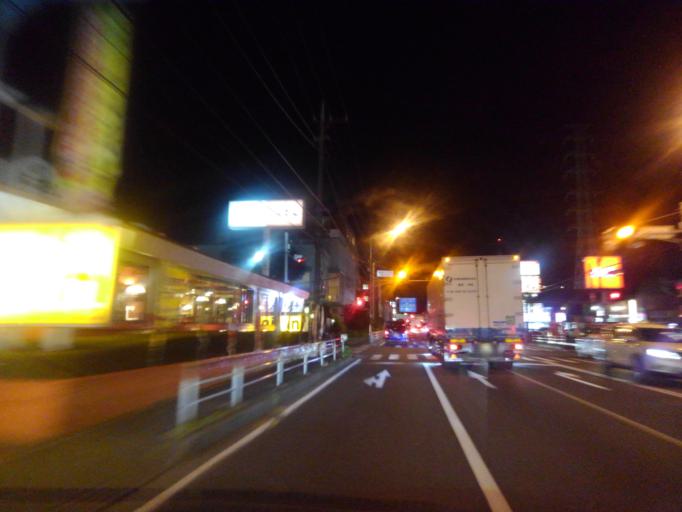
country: JP
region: Tokyo
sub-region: Machida-shi
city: Machida
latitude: 35.5635
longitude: 139.3942
